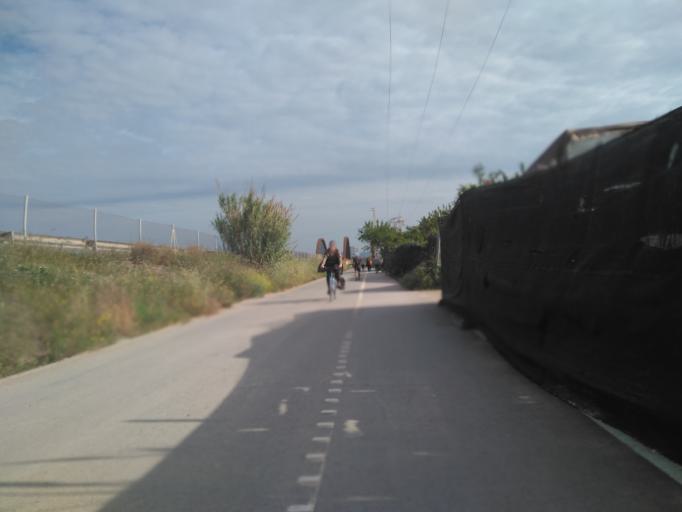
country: ES
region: Valencia
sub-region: Provincia de Valencia
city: Alboraya
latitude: 39.5000
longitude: -0.3254
